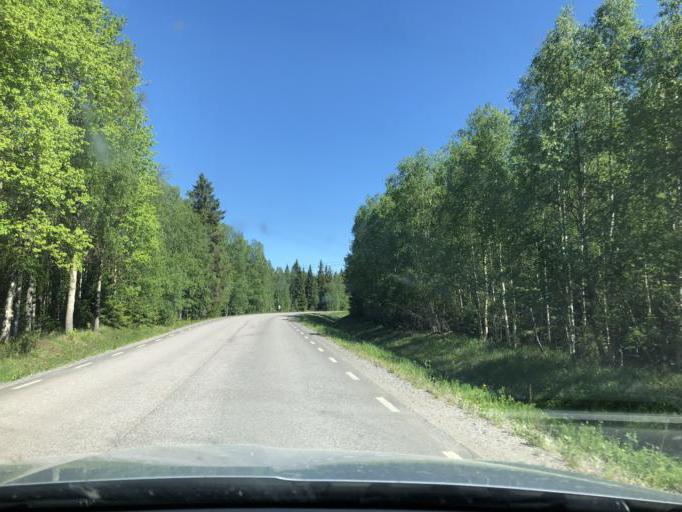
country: SE
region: Norrbotten
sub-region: Lulea Kommun
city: Gammelstad
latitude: 65.6522
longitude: 22.0331
